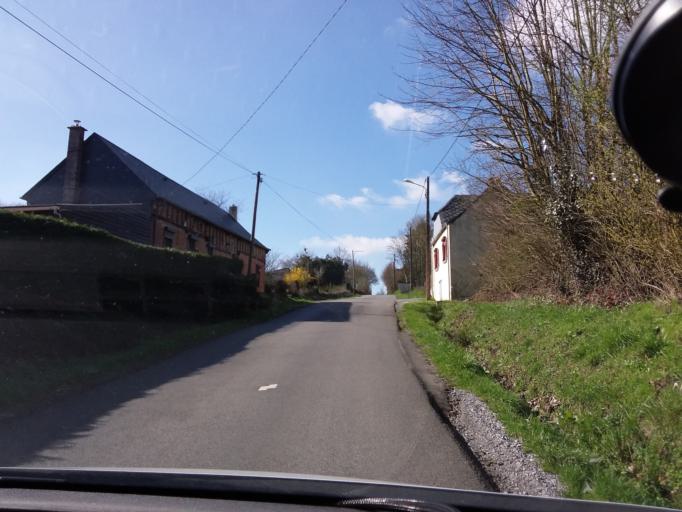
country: FR
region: Picardie
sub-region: Departement de l'Aisne
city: Origny-en-Thierache
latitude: 49.8472
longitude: 4.0761
